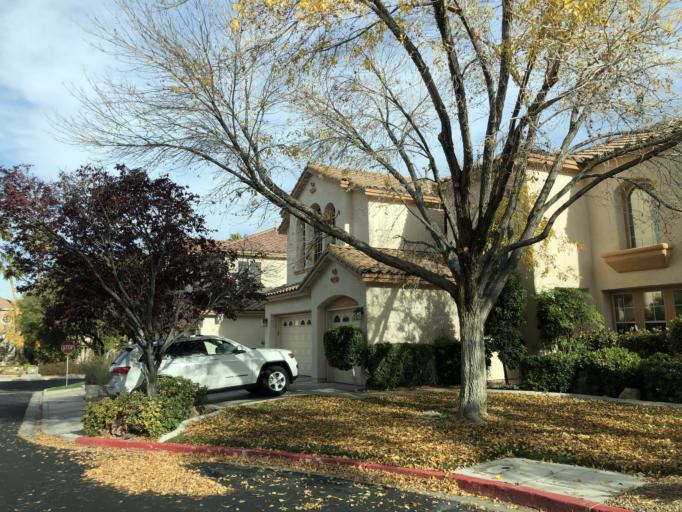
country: US
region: Nevada
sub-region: Clark County
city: Whitney
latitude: 36.0184
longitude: -115.0748
